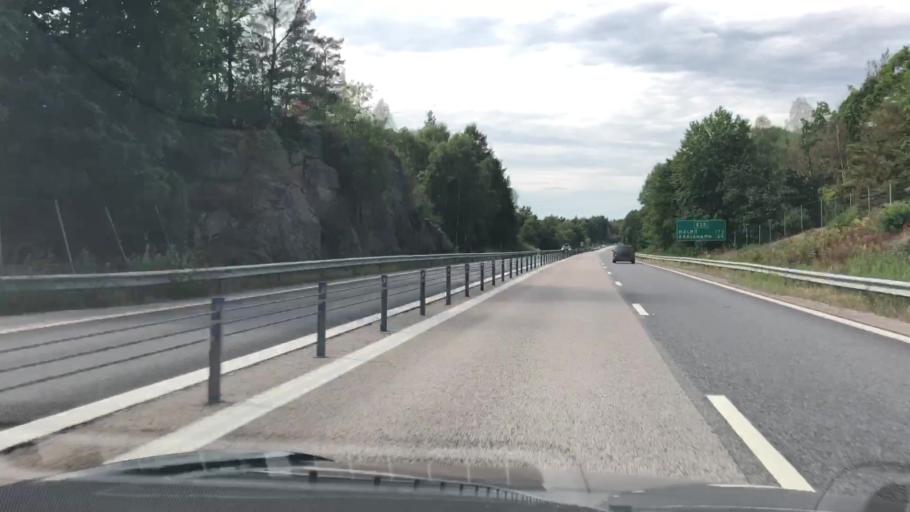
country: SE
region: Blekinge
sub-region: Ronneby Kommun
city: Ronneby
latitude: 56.2202
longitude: 15.2063
